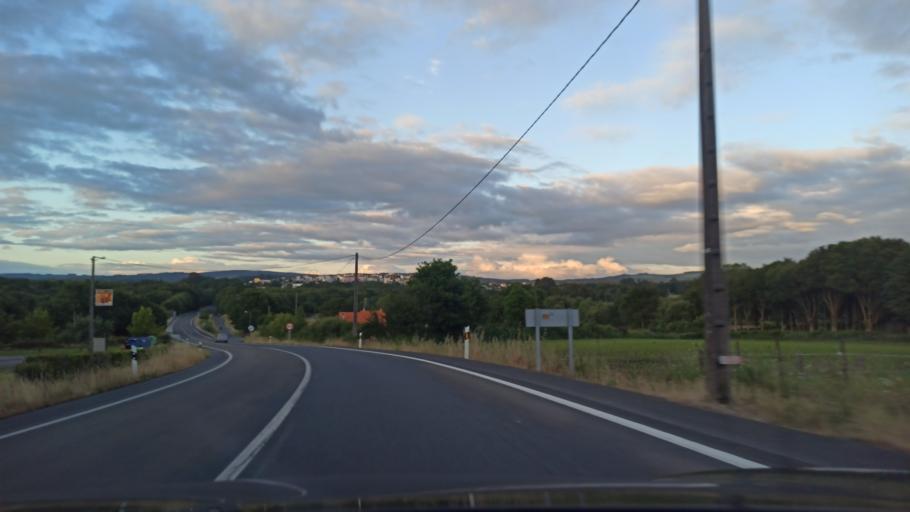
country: ES
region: Galicia
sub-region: Provincia de Lugo
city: Monterroso
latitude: 42.7887
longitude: -7.8608
